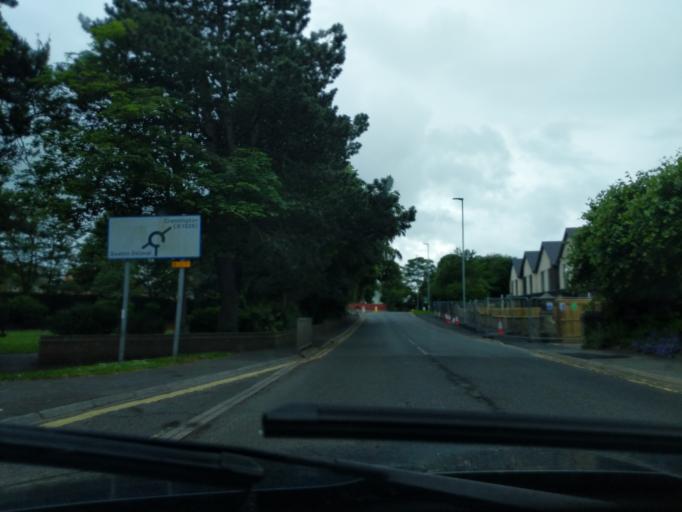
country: GB
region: England
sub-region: Northumberland
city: Seaton Delaval
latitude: 55.0766
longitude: -1.5370
